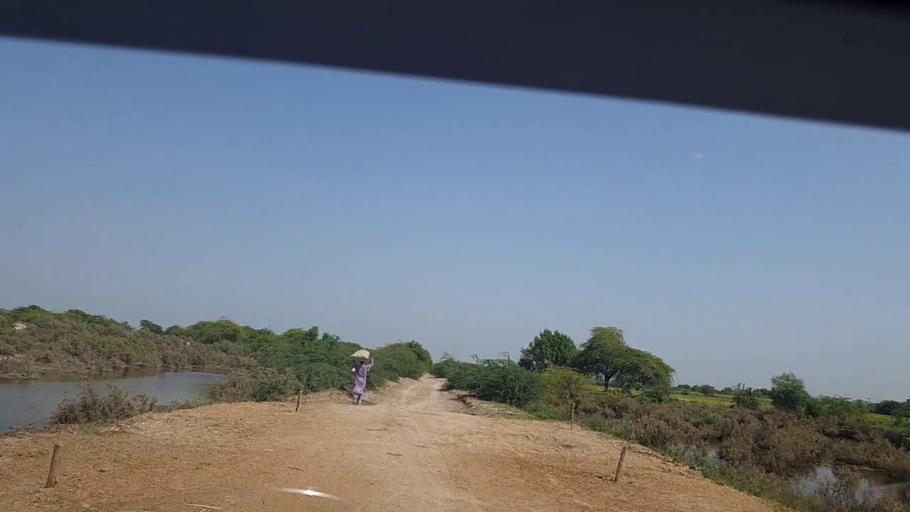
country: PK
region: Sindh
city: Rajo Khanani
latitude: 24.9607
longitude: 68.8666
